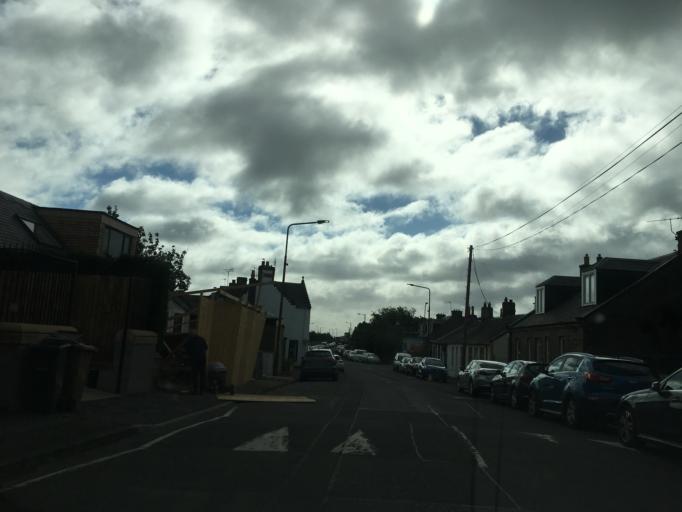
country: GB
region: Scotland
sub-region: Edinburgh
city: Newbridge
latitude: 55.9392
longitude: -3.4093
